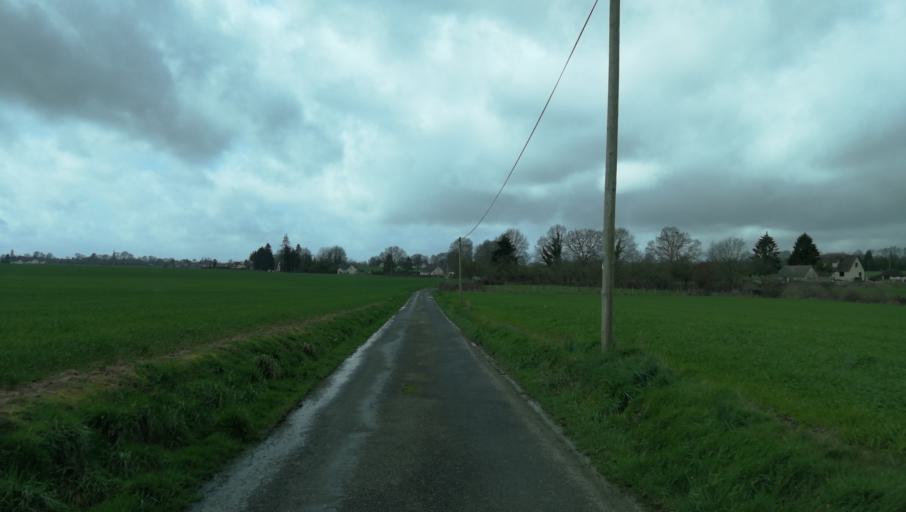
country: FR
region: Haute-Normandie
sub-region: Departement de l'Eure
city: Lieurey
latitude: 49.2353
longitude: 0.5197
